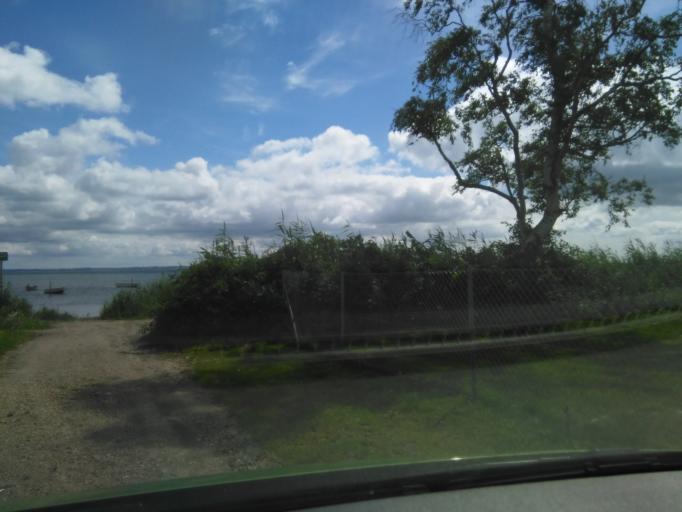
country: DK
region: Central Jutland
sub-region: Arhus Kommune
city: Logten
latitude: 56.2604
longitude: 10.3435
